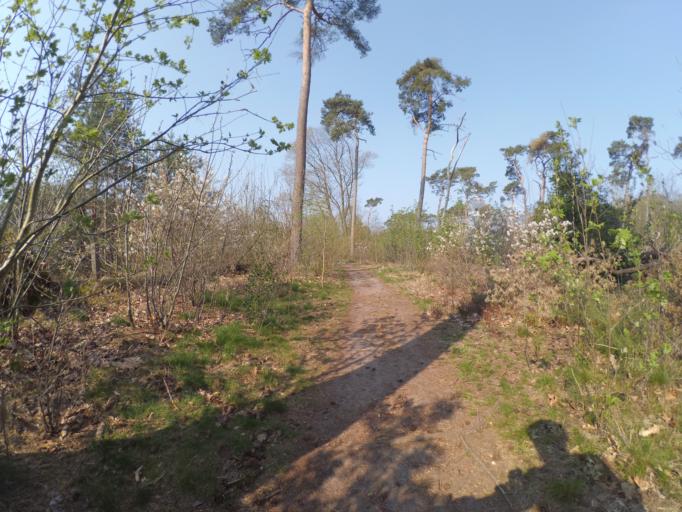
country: NL
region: Utrecht
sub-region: Gemeente Amersfoort
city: Amersfoort
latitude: 52.1328
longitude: 5.3785
